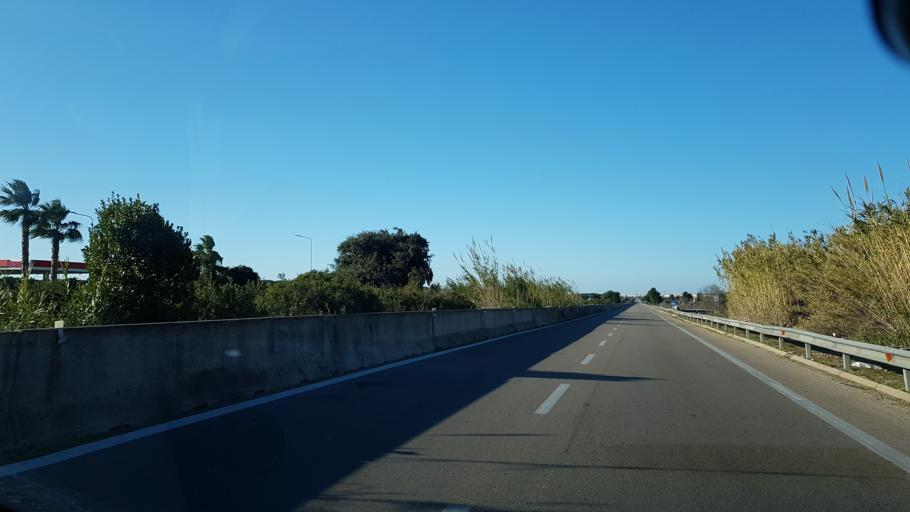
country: IT
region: Apulia
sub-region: Provincia di Lecce
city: Alezio
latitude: 40.0174
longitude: 18.0457
